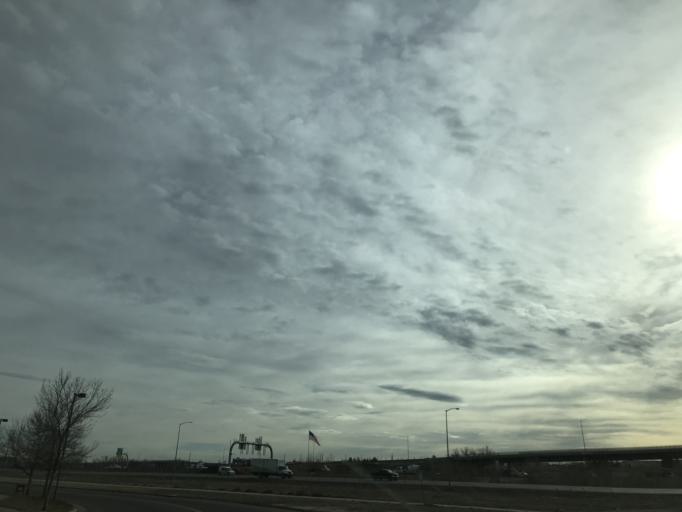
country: US
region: Colorado
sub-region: Adams County
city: Commerce City
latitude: 39.7801
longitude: -104.8963
